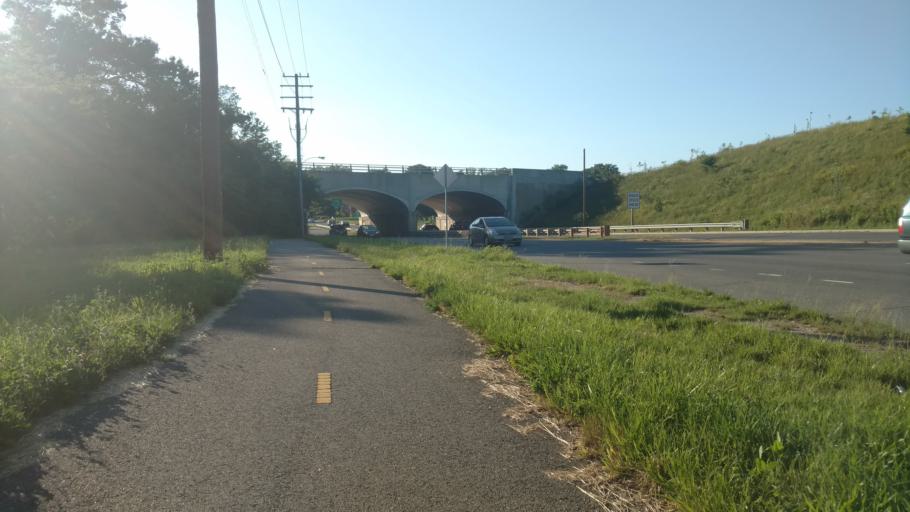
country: US
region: Virginia
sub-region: Arlington County
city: Arlington
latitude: 38.8746
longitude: -77.0831
